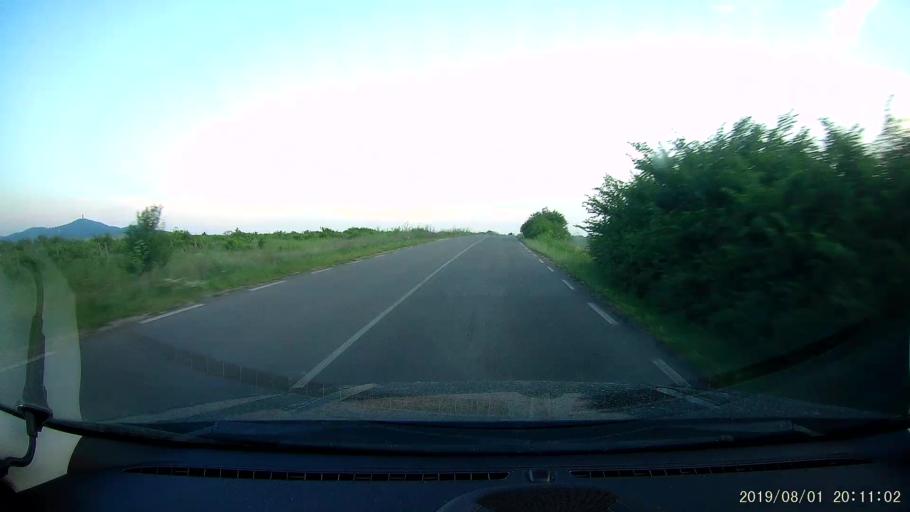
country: BG
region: Yambol
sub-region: Obshtina Yambol
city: Yambol
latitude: 42.4694
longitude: 26.6049
